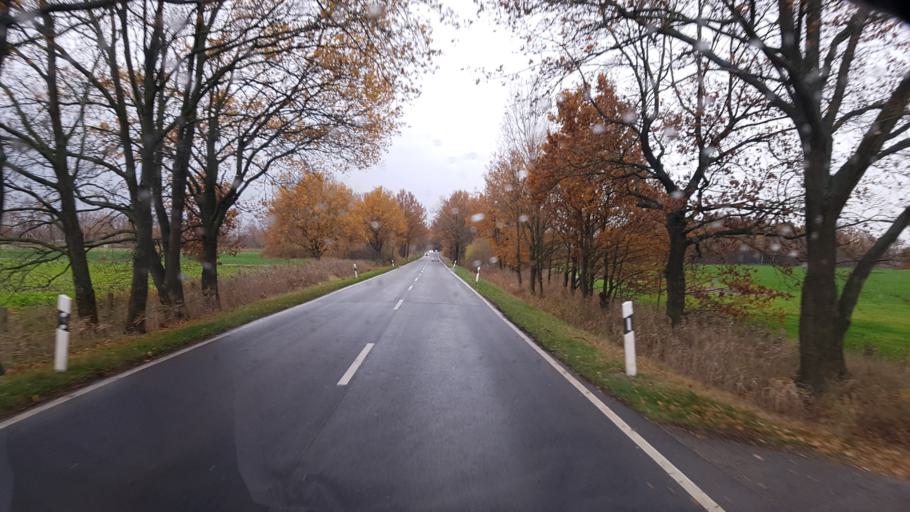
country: DE
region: Brandenburg
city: Schraden
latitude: 51.4633
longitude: 13.7123
